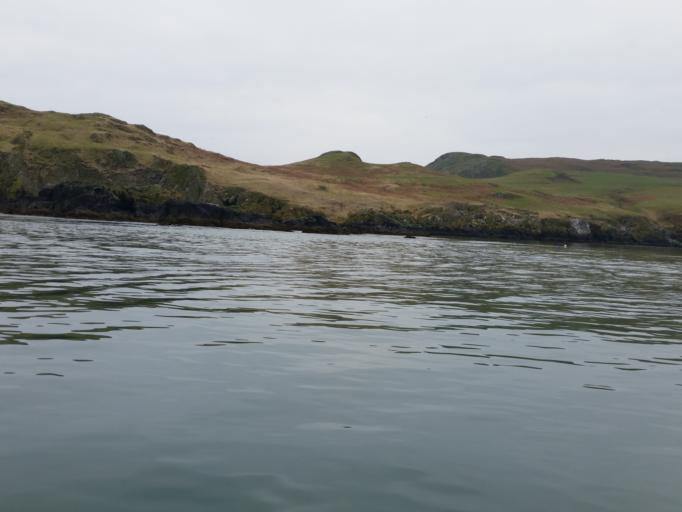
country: IE
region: Leinster
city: An Ros
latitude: 53.4973
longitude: -5.9964
